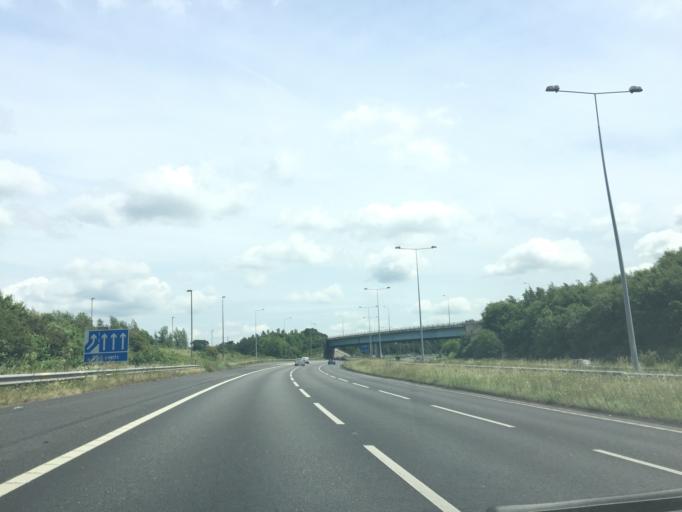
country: GB
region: England
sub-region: Medway
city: Cuxton
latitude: 51.3997
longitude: 0.4468
